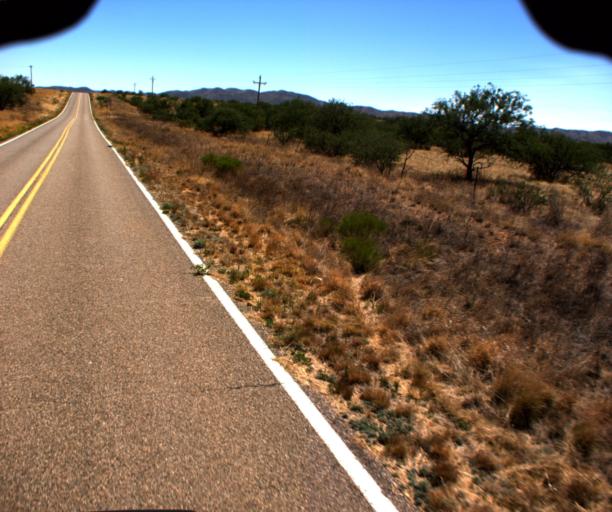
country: US
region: Arizona
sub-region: Pima County
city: Sells
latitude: 31.5875
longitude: -111.5323
